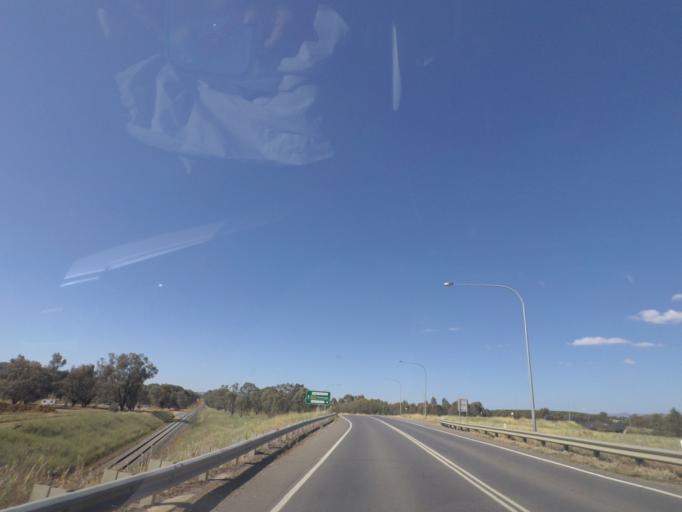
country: AU
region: New South Wales
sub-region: Albury Municipality
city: Lavington
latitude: -36.0023
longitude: 146.9895
